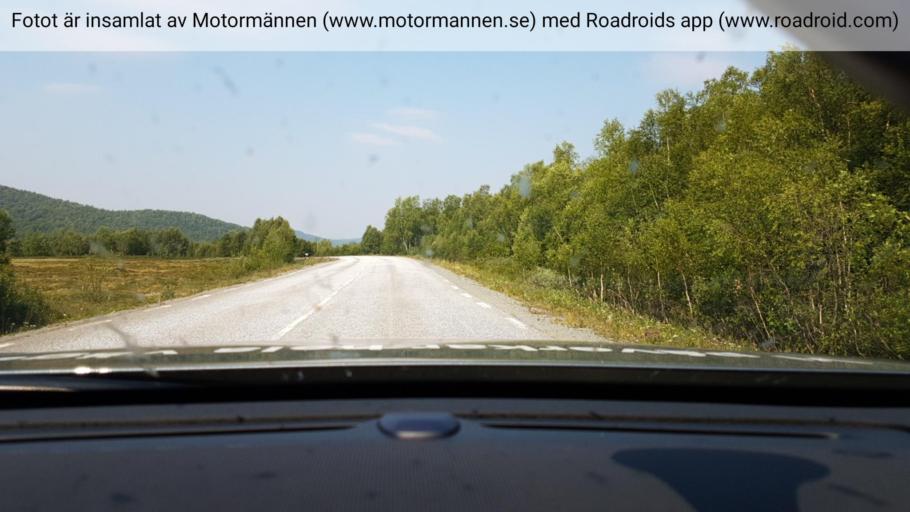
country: NO
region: Nordland
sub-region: Rana
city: Mo i Rana
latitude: 65.7825
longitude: 15.1178
